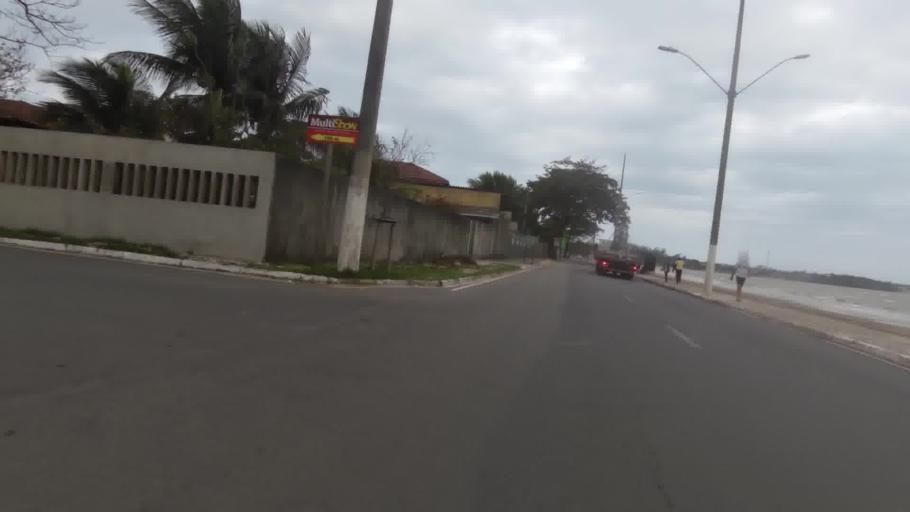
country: BR
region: Espirito Santo
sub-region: Piuma
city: Piuma
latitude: -20.8098
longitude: -40.6412
